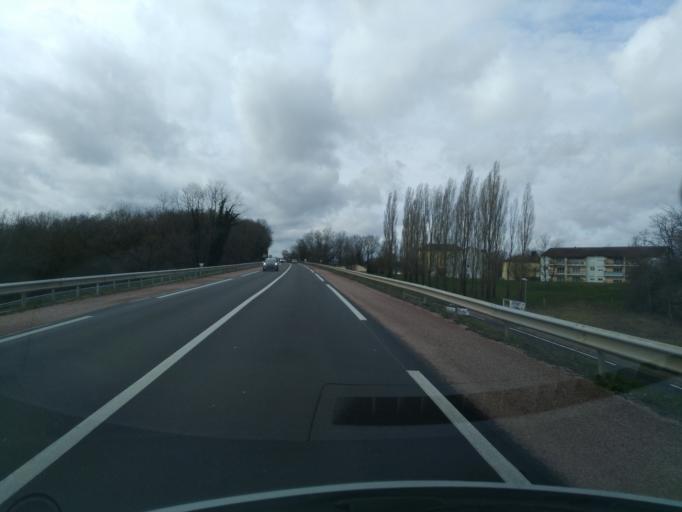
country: FR
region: Bourgogne
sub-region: Departement de Saone-et-Loire
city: Montchanin
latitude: 46.7567
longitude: 4.4775
